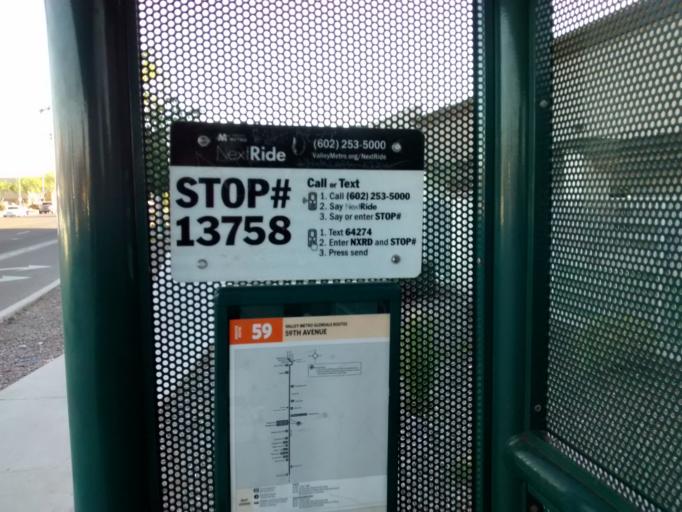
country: US
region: Arizona
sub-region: Maricopa County
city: Peoria
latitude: 33.6103
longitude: -112.1860
